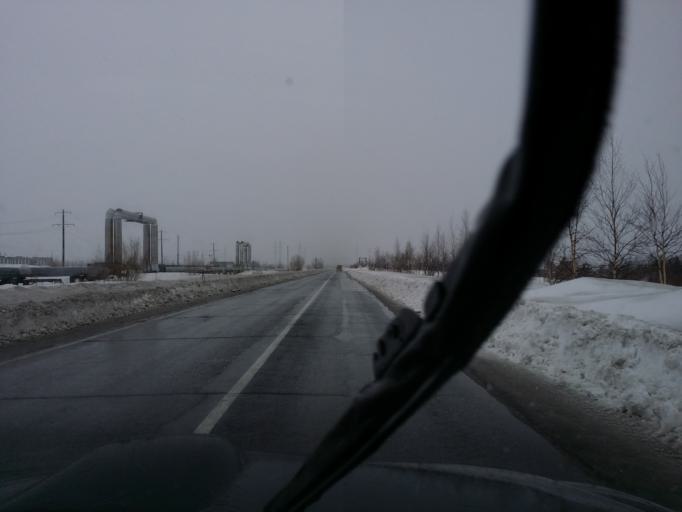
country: RU
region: Khanty-Mansiyskiy Avtonomnyy Okrug
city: Izluchinsk
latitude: 60.9779
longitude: 76.9000
